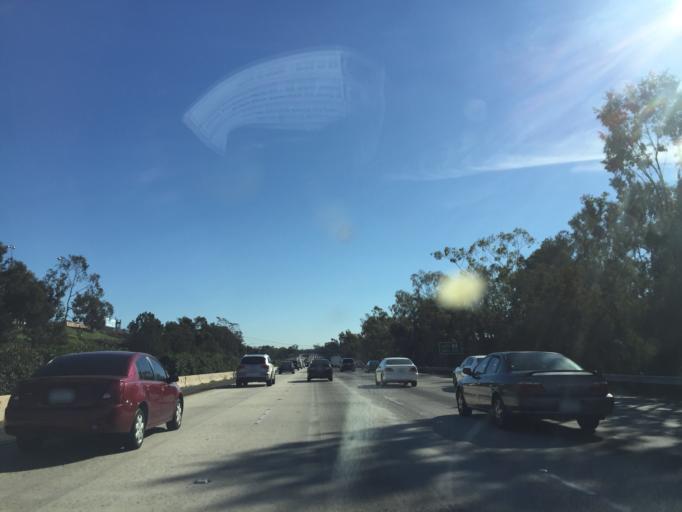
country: US
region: California
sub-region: San Diego County
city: Encinitas
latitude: 33.0551
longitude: -117.2894
